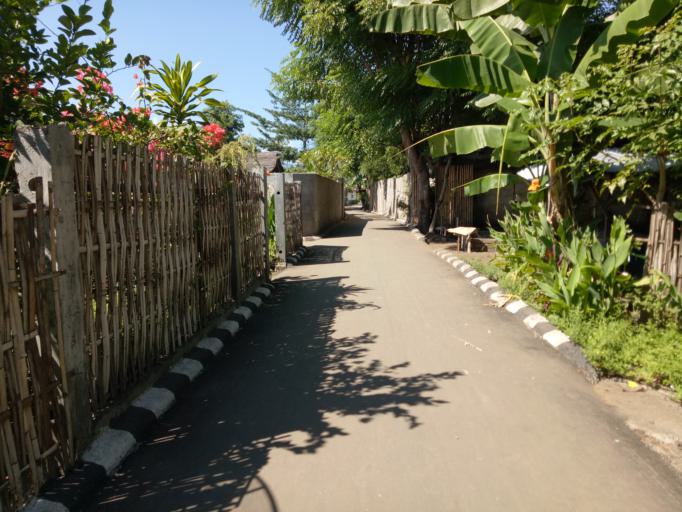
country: ID
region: West Nusa Tenggara
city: Gili Air
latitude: -8.3599
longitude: 116.0813
